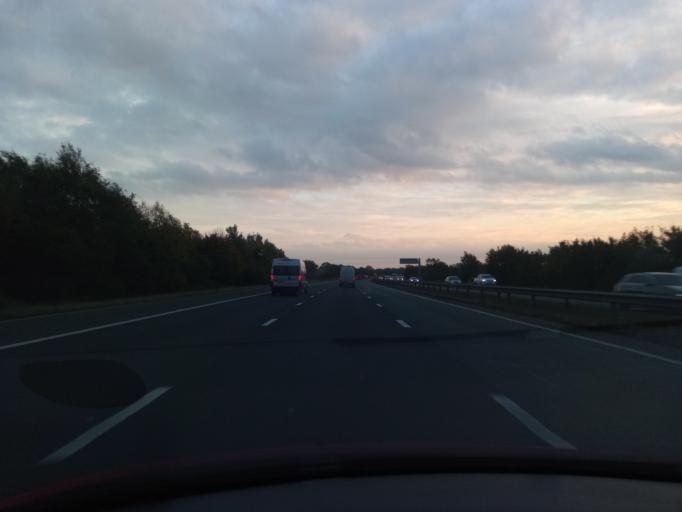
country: GB
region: England
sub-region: City and Borough of Leeds
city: Wetherby
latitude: 53.9982
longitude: -1.3660
